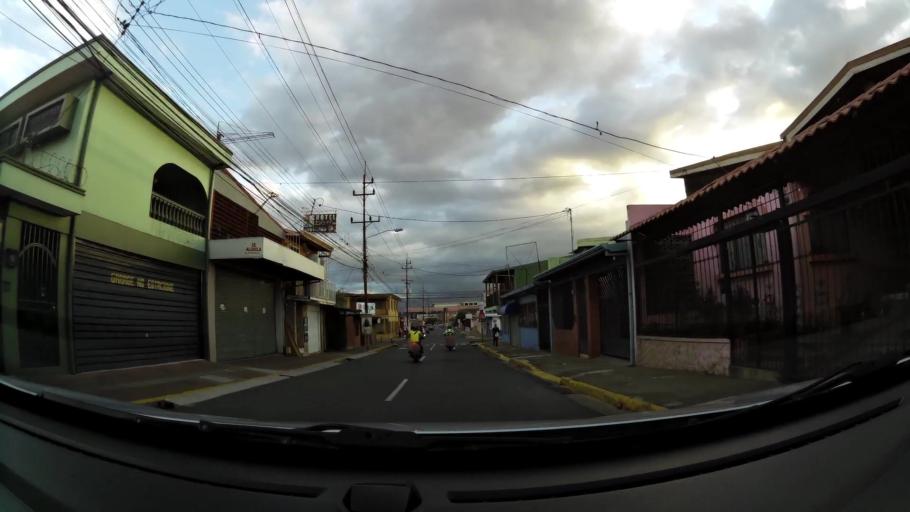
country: CR
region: Heredia
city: Heredia
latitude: 9.9964
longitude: -84.1218
